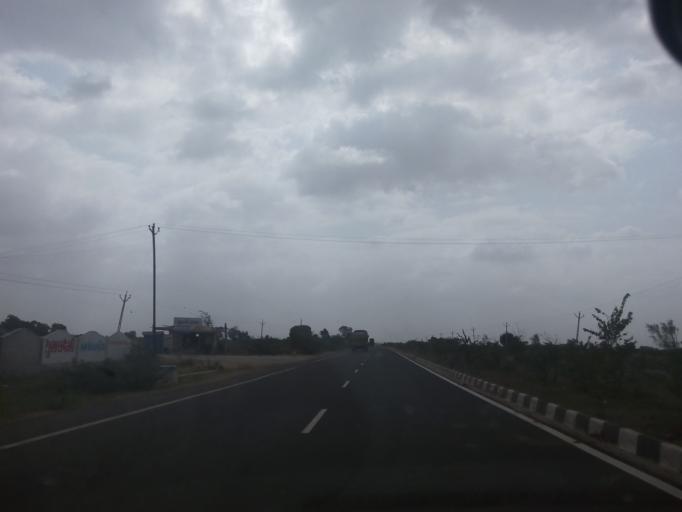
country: IN
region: Gujarat
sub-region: Surendranagar
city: Halvad
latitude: 23.0049
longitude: 71.1414
